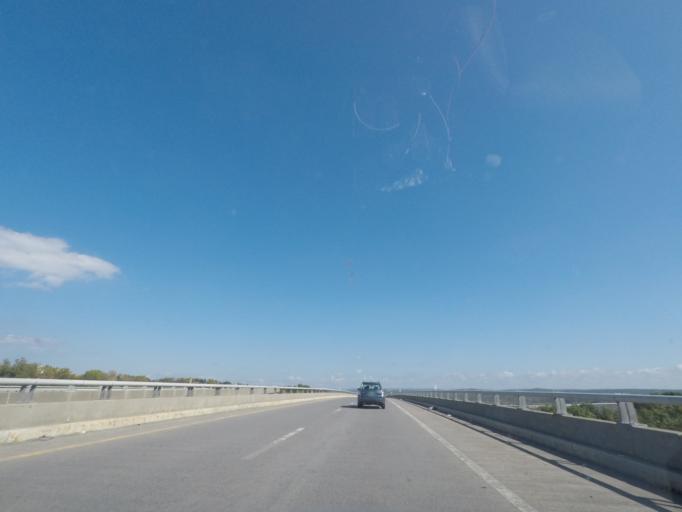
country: US
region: New York
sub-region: Albany County
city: Albany
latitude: 42.6673
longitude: -73.7522
